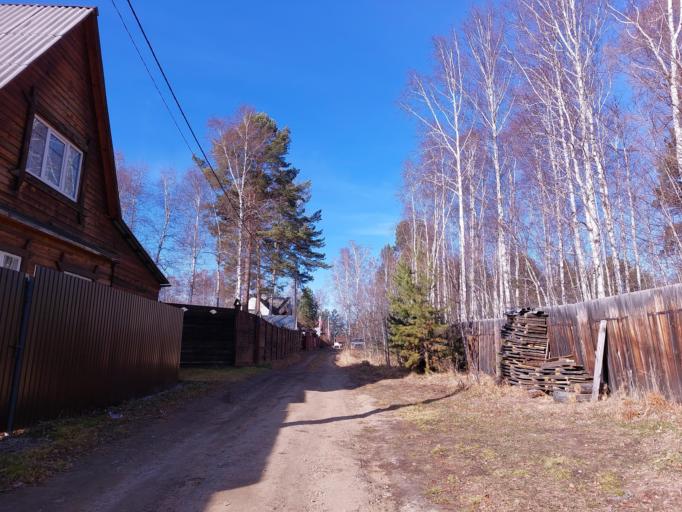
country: RU
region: Irkutsk
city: Pivovarikha
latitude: 52.1862
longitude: 104.4555
